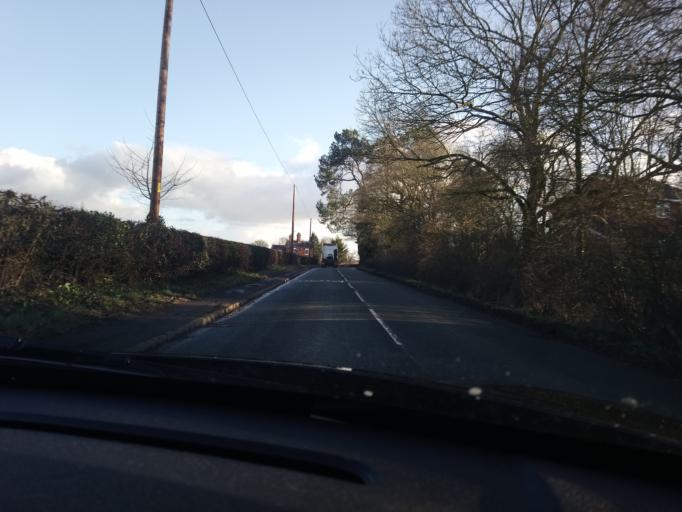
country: GB
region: England
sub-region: Shropshire
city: Ellesmere
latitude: 52.9153
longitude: -2.9149
